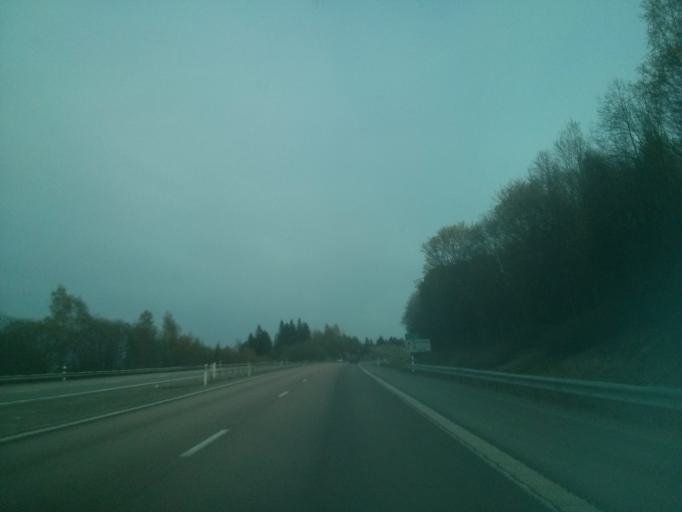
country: SE
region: Vaesternorrland
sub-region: Timra Kommun
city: Timra
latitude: 62.4663
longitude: 17.3279
